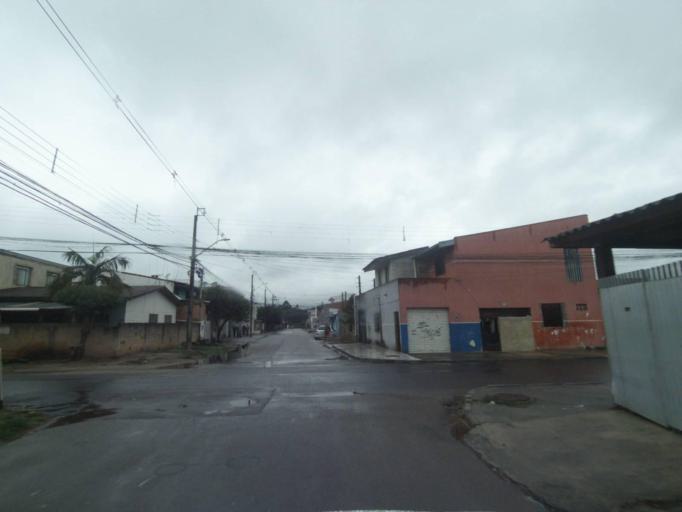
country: BR
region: Parana
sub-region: Araucaria
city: Araucaria
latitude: -25.5317
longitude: -49.3404
